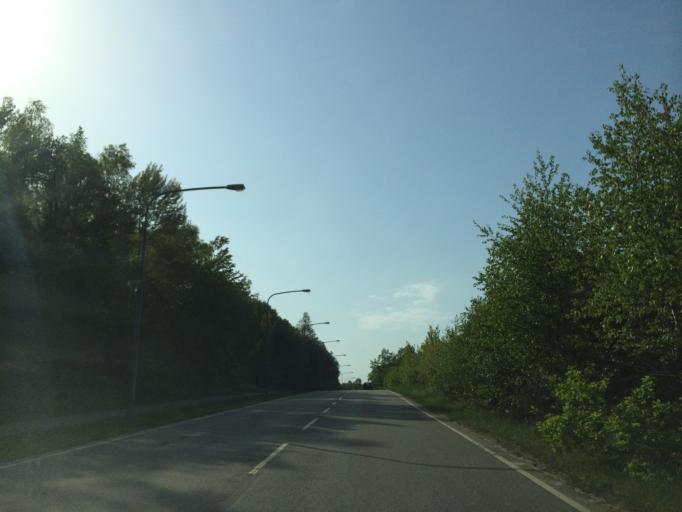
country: SE
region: Stockholm
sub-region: Nacka Kommun
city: Alta
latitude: 59.2619
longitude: 18.1515
